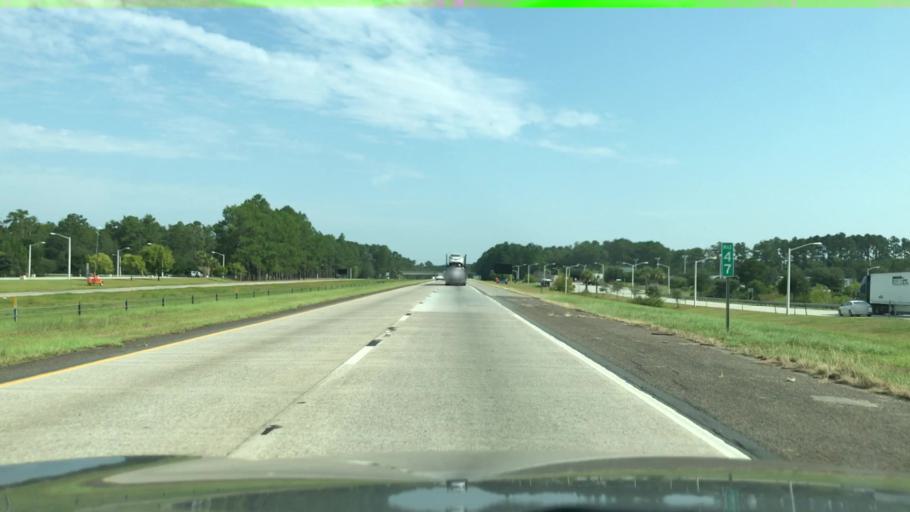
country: US
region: South Carolina
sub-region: Hampton County
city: Yemassee
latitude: 32.7987
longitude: -80.7724
